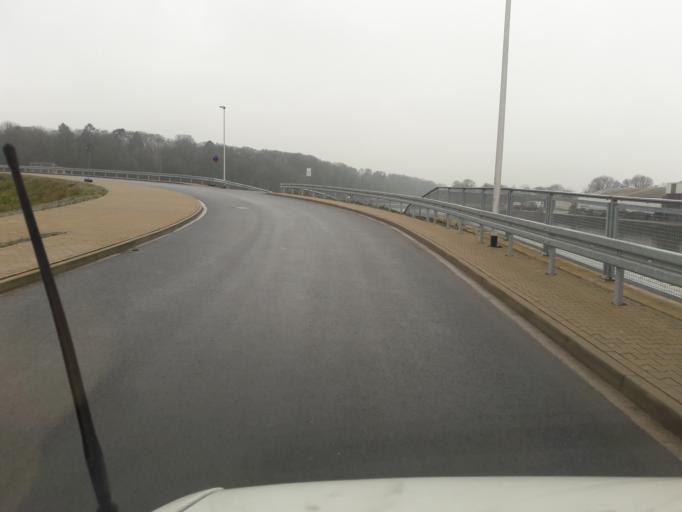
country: DE
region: North Rhine-Westphalia
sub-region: Regierungsbezirk Detmold
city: Minden
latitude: 52.3066
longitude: 8.9222
